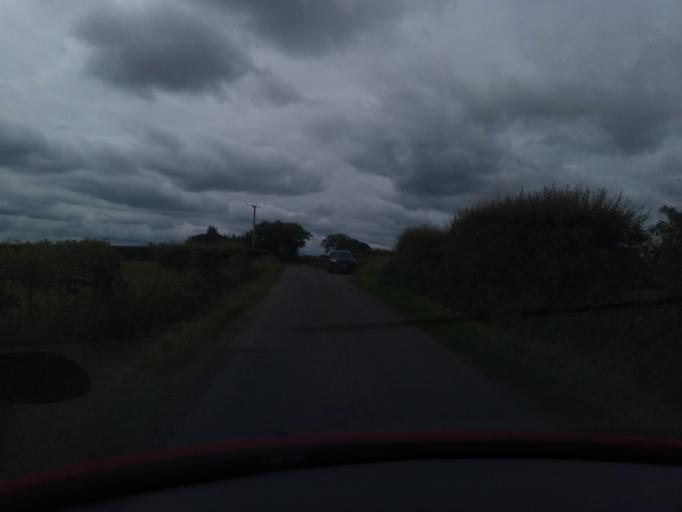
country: GB
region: Scotland
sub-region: The Scottish Borders
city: Hawick
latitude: 55.4491
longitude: -2.8000
